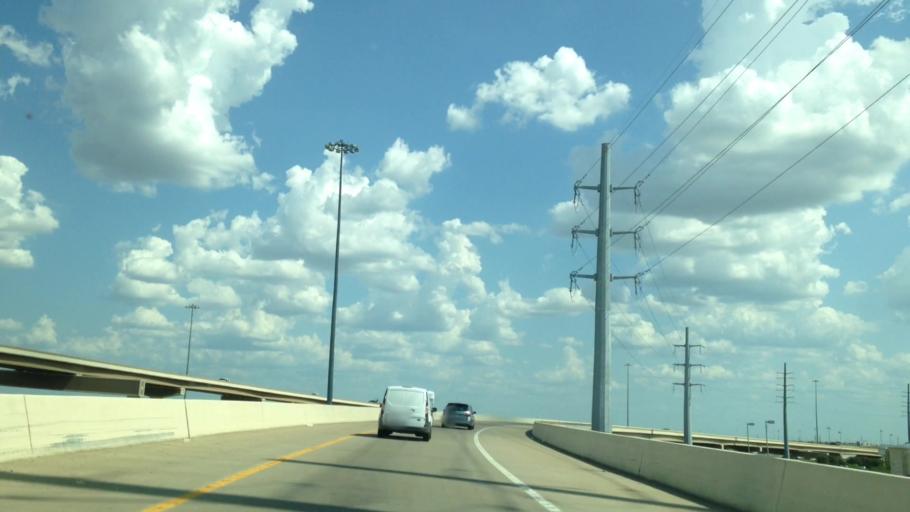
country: US
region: Texas
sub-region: Travis County
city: Pflugerville
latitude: 30.4745
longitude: -97.5951
